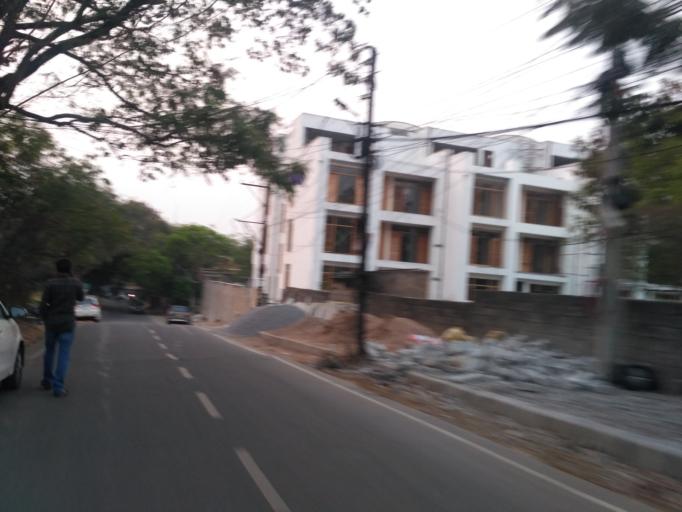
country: IN
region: Telangana
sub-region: Rangareddi
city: Kukatpalli
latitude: 17.4383
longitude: 78.4013
